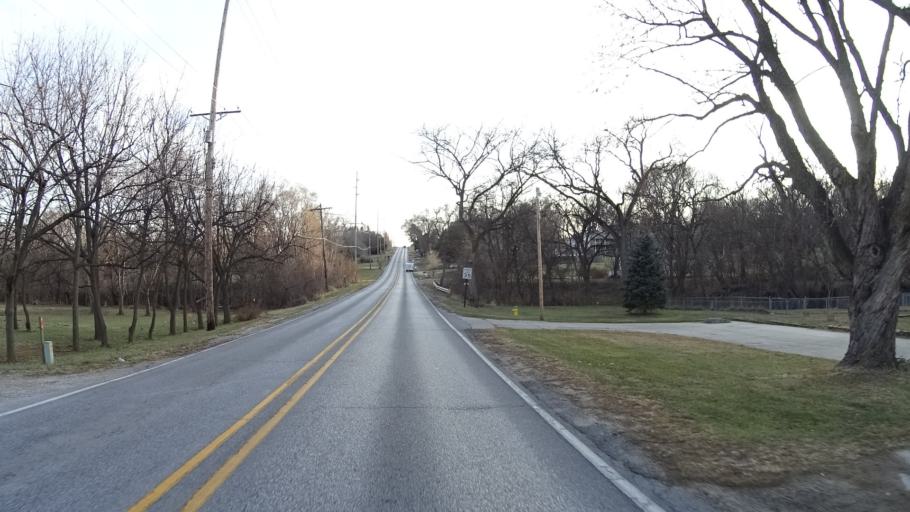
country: US
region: Nebraska
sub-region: Sarpy County
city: La Vista
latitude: 41.1756
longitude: -95.9673
